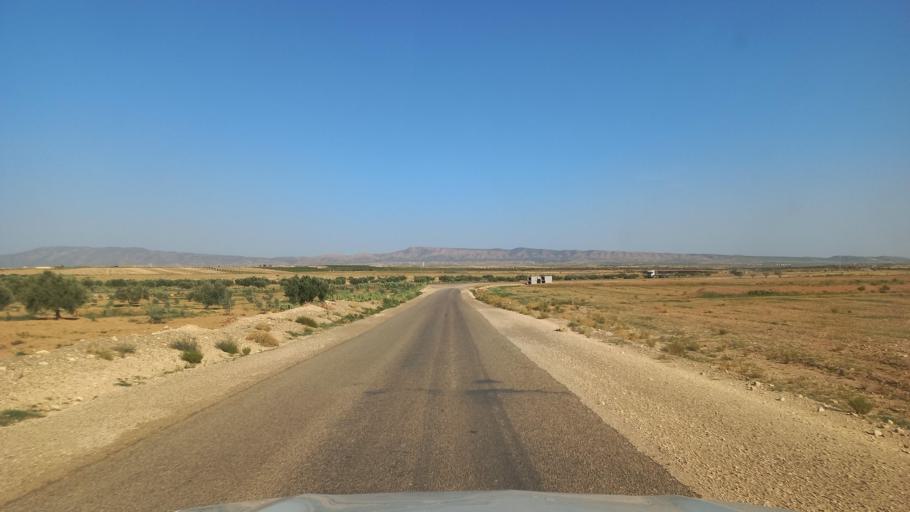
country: TN
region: Al Qasrayn
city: Sbiba
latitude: 35.3779
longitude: 9.0298
